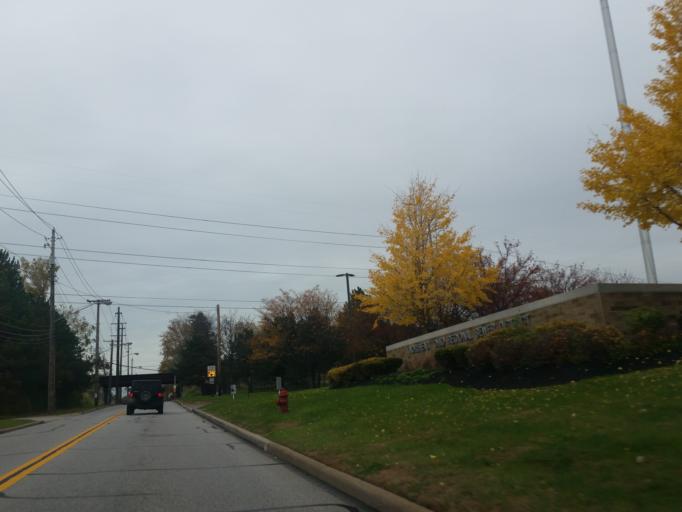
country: US
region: Ohio
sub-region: Cuyahoga County
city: Newburgh Heights
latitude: 41.4295
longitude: -81.6566
